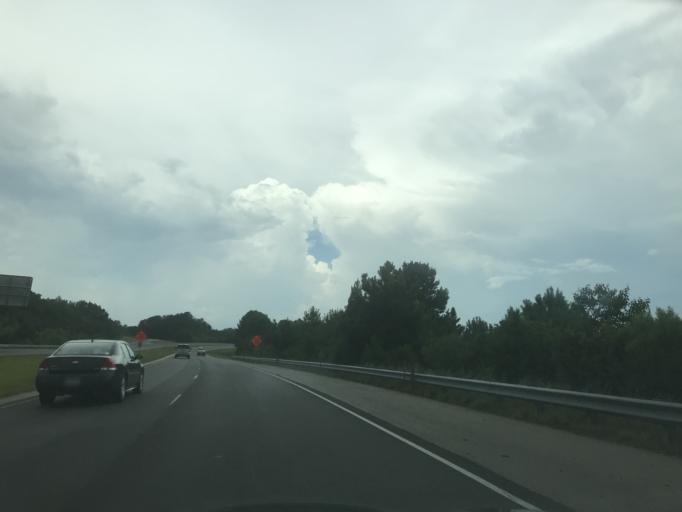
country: US
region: North Carolina
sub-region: Johnston County
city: Wilsons Mills
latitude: 35.6000
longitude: -78.4124
